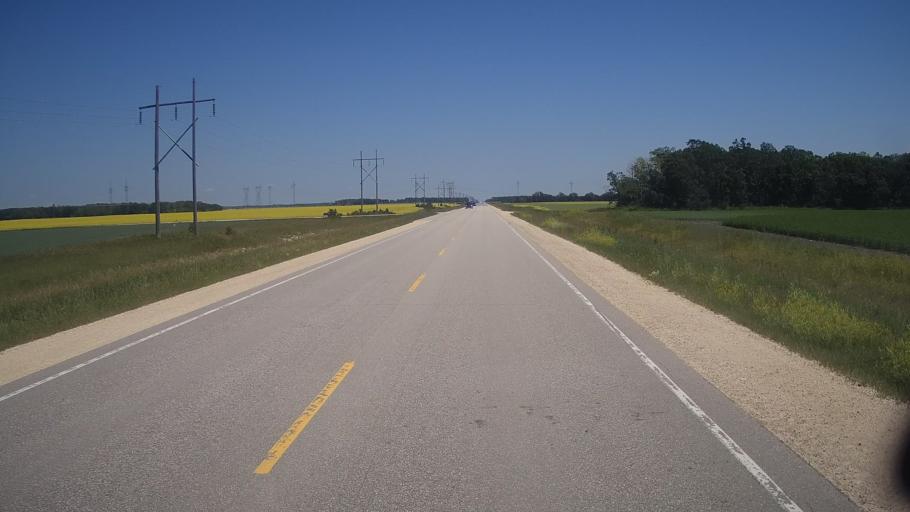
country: CA
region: Manitoba
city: Stonewall
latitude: 50.1227
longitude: -97.5078
